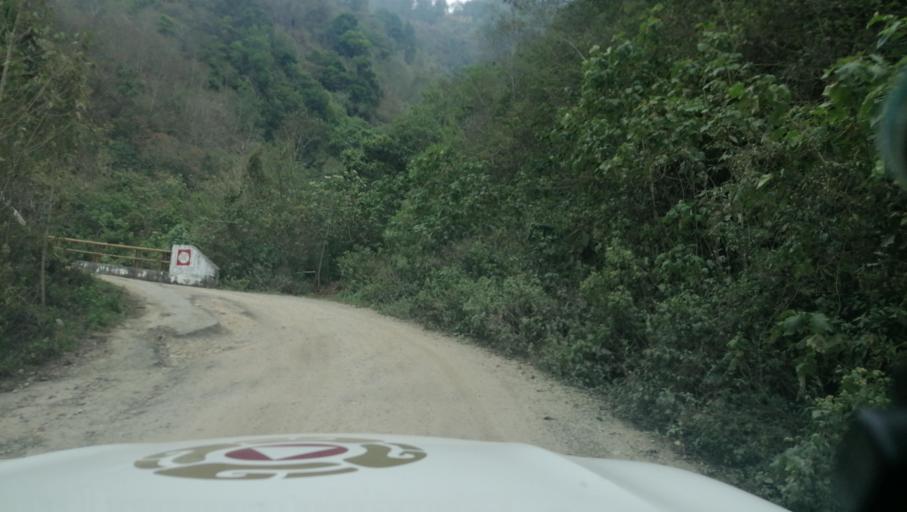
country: GT
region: San Marcos
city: Tacana
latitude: 15.2221
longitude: -92.1967
